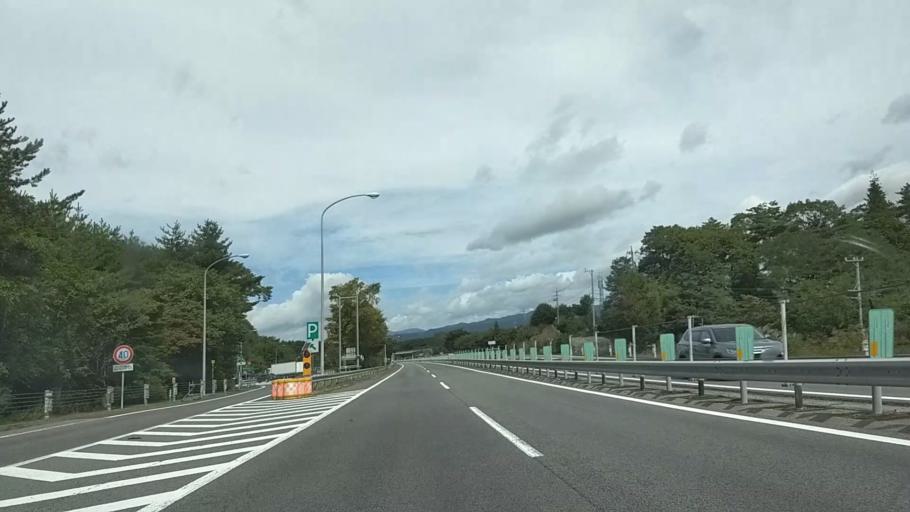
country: JP
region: Nagano
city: Chino
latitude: 35.9531
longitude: 138.1985
